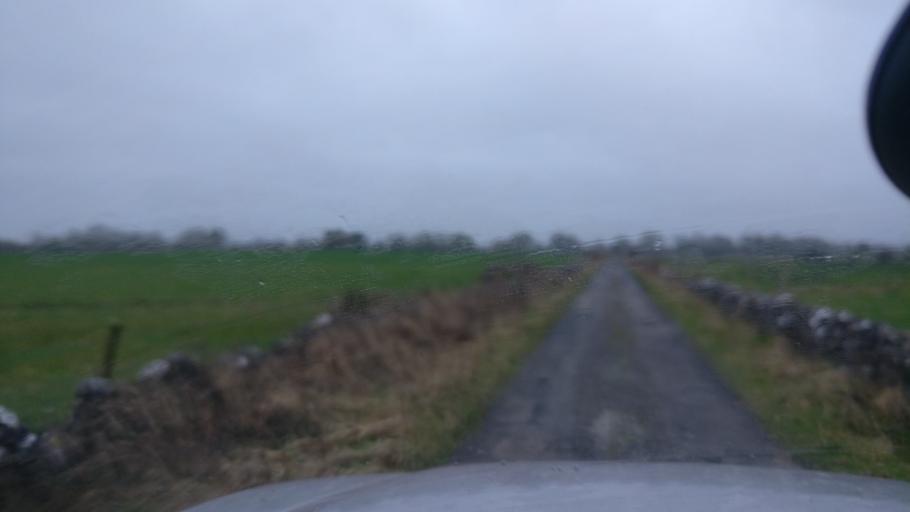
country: IE
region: Connaught
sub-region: County Galway
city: Loughrea
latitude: 53.2301
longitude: -8.5950
